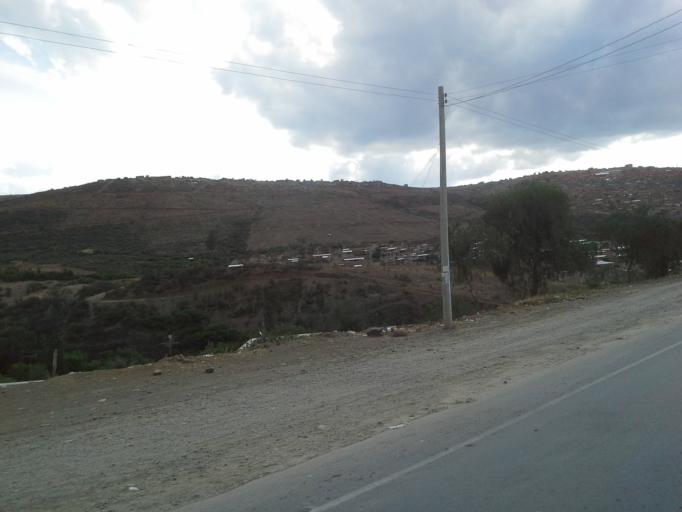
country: BO
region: Cochabamba
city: Cochabamba
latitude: -17.4842
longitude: -66.1033
